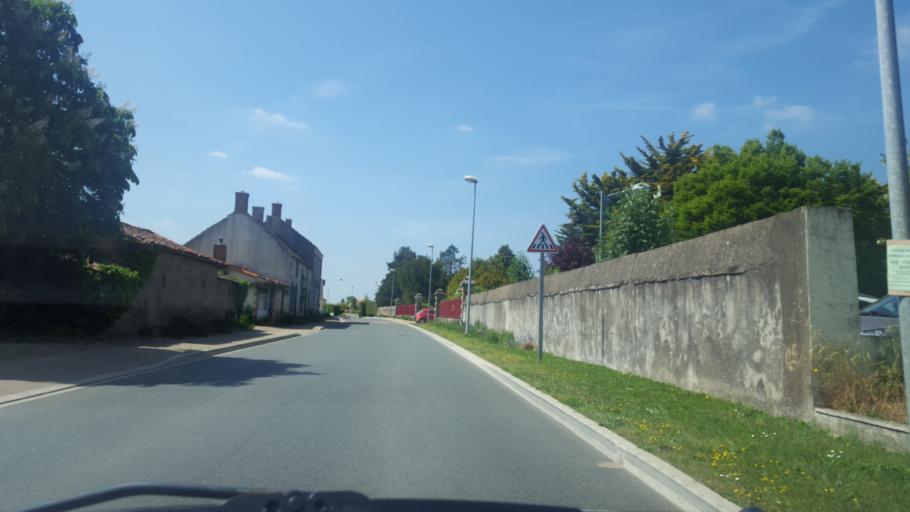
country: FR
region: Pays de la Loire
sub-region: Departement de la Loire-Atlantique
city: La Limouziniere
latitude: 46.9580
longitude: -1.5665
